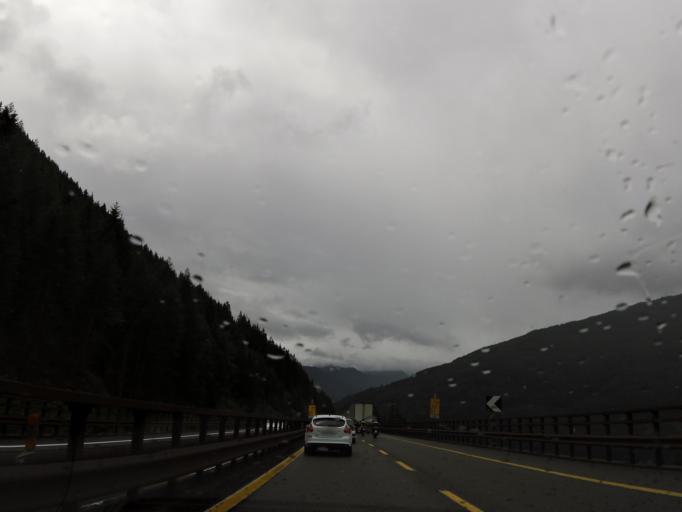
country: IT
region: Trentino-Alto Adige
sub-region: Bolzano
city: Colle Isarco
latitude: 46.9466
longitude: 11.4521
